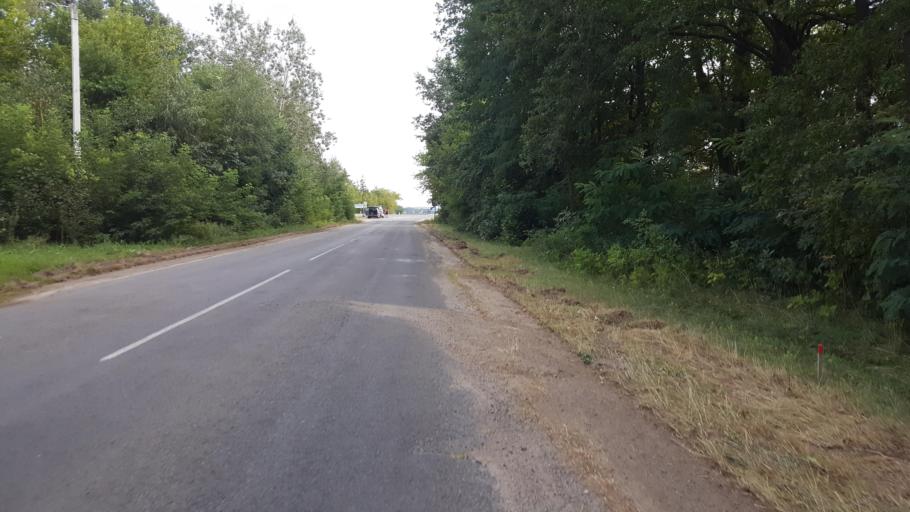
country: BY
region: Brest
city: Kamyanyets
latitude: 52.4133
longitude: 23.7870
